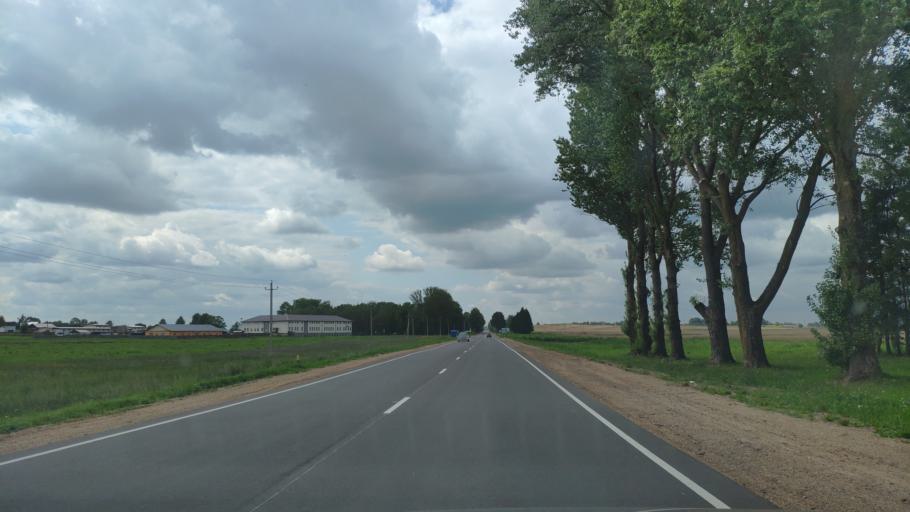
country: BY
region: Minsk
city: Zaslawye
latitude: 54.0060
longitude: 27.3380
